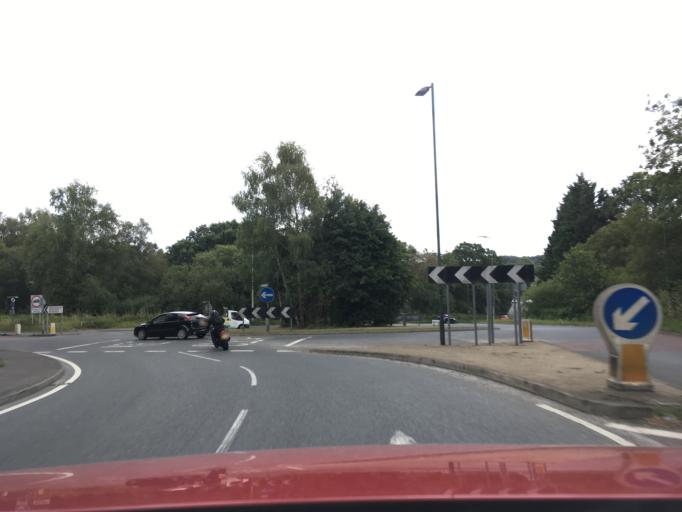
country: GB
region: England
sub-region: West Berkshire
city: Thatcham
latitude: 51.3693
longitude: -1.2752
